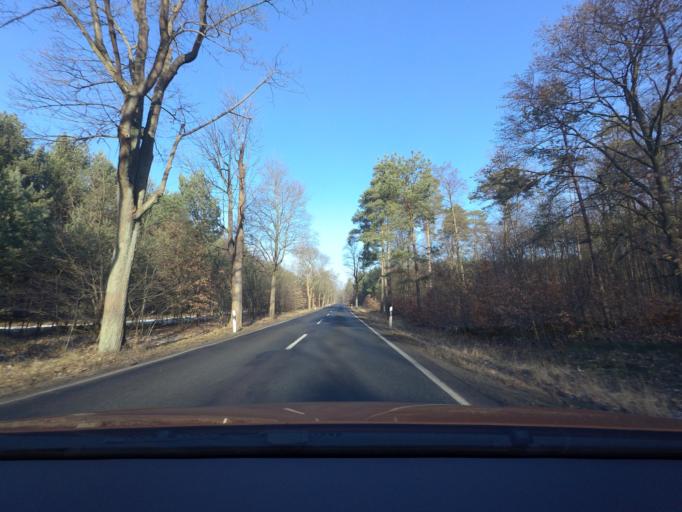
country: DE
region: Brandenburg
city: Wandlitz
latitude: 52.7253
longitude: 13.3678
